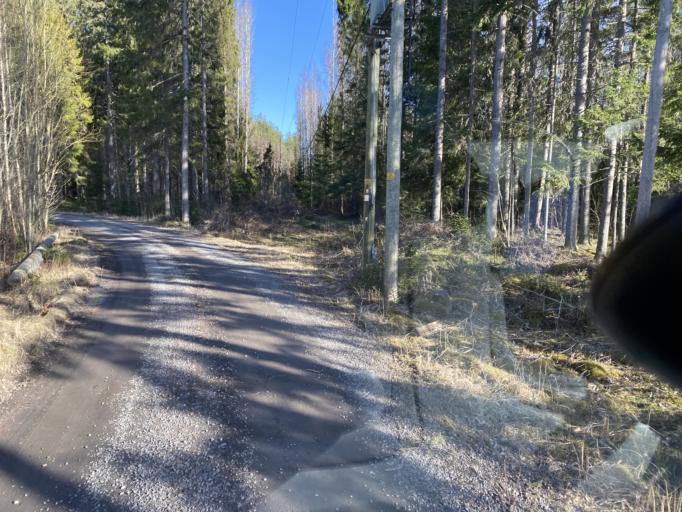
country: FI
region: Satakunta
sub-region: Rauma
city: Lappi
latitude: 61.1499
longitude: 21.8823
